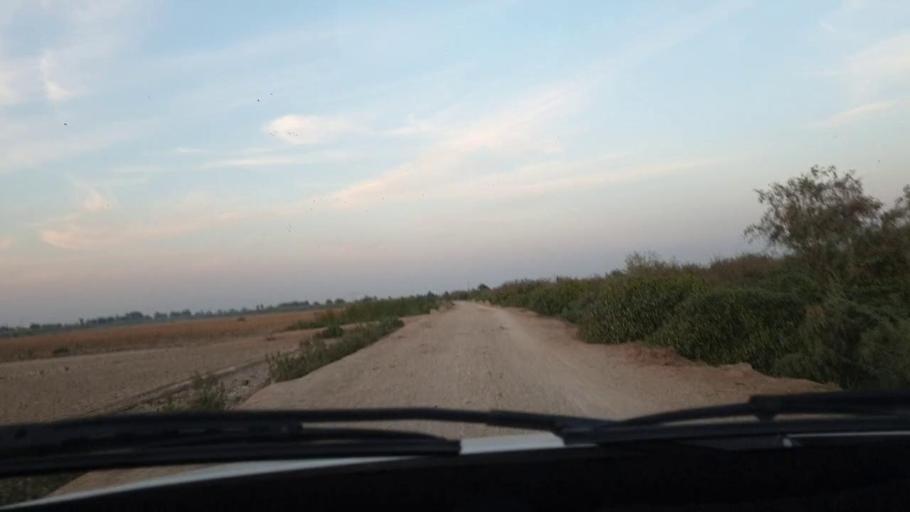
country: PK
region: Sindh
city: Tando Muhammad Khan
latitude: 25.0937
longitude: 68.3879
